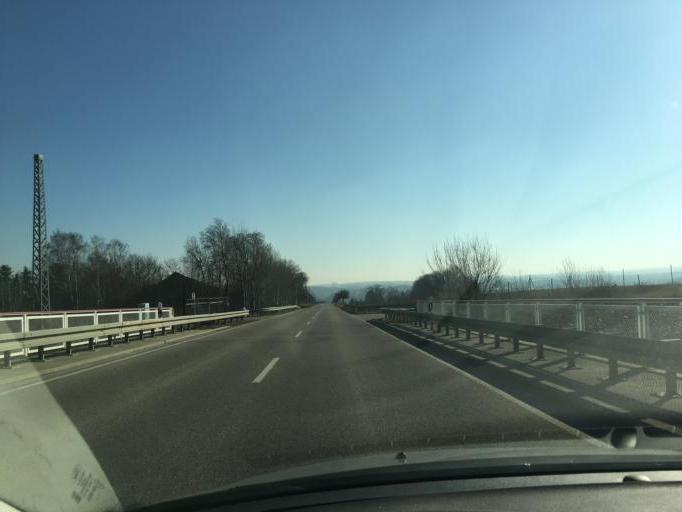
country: DE
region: Saxony
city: Penig
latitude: 50.9420
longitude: 12.6879
